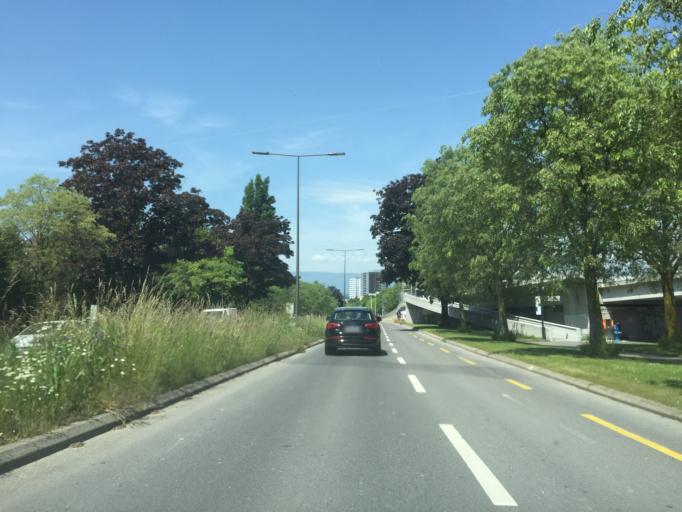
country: CH
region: Vaud
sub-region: Lausanne District
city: Lausanne
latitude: 46.5214
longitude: 6.6142
